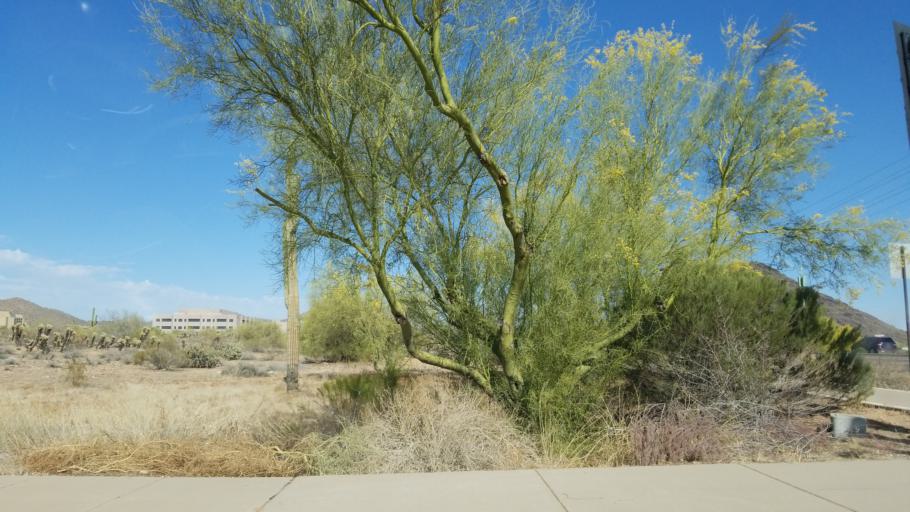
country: US
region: Arizona
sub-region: Maricopa County
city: Fountain Hills
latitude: 33.5826
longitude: -111.8003
